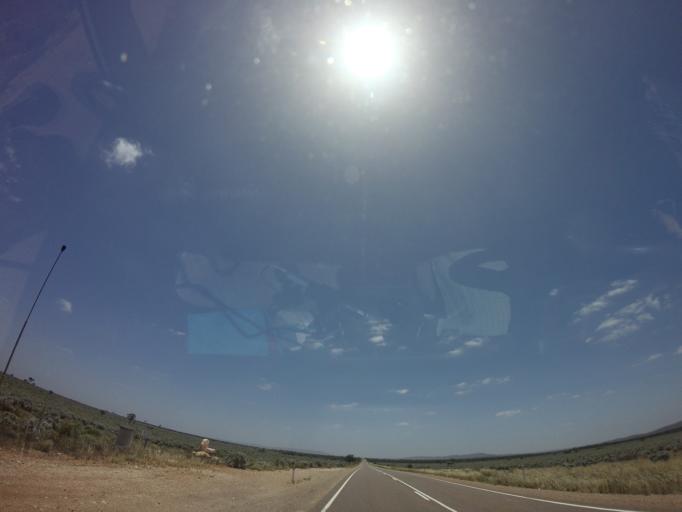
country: AU
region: South Australia
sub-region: Whyalla
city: Whyalla
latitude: -32.8368
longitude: 137.0289
